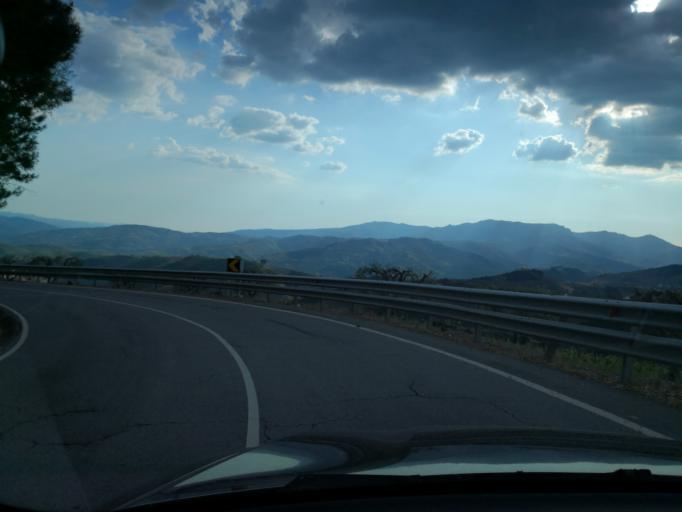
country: PT
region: Vila Real
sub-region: Vila Real
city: Vila Real
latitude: 41.2437
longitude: -7.7269
